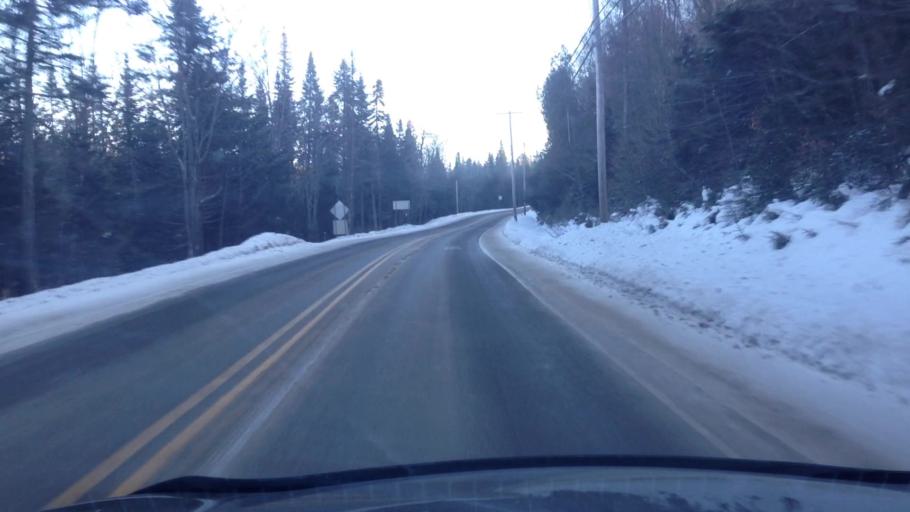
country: CA
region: Quebec
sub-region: Laurentides
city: Sainte-Agathe-des-Monts
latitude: 45.9104
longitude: -74.3503
